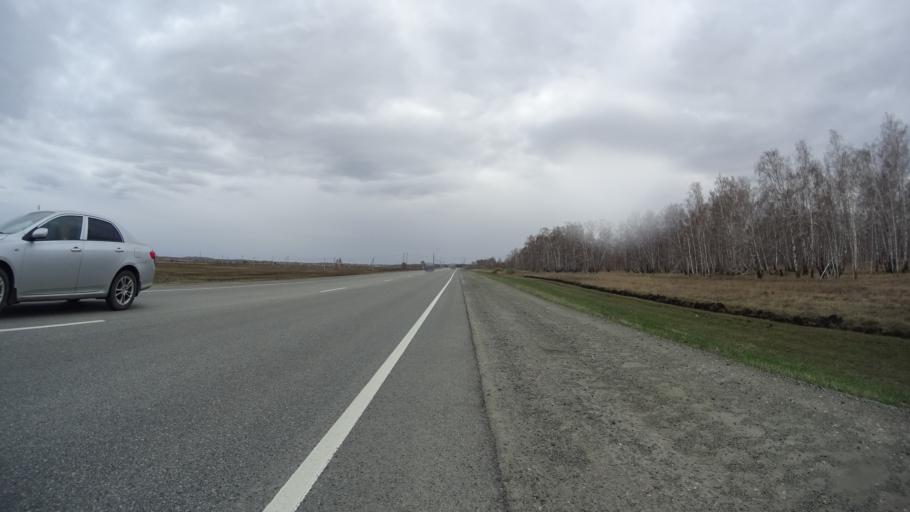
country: RU
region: Chelyabinsk
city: Krasnogorskiy
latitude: 54.6879
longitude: 61.2481
